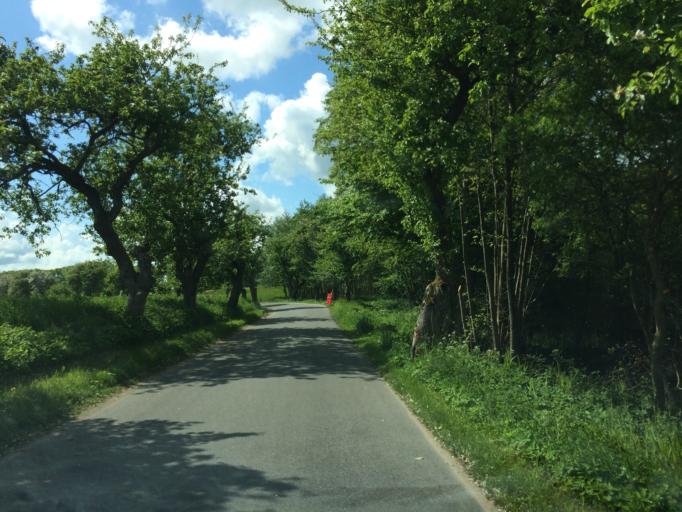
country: DK
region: Zealand
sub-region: Lejre Kommune
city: Lejre
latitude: 55.6087
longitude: 11.9430
